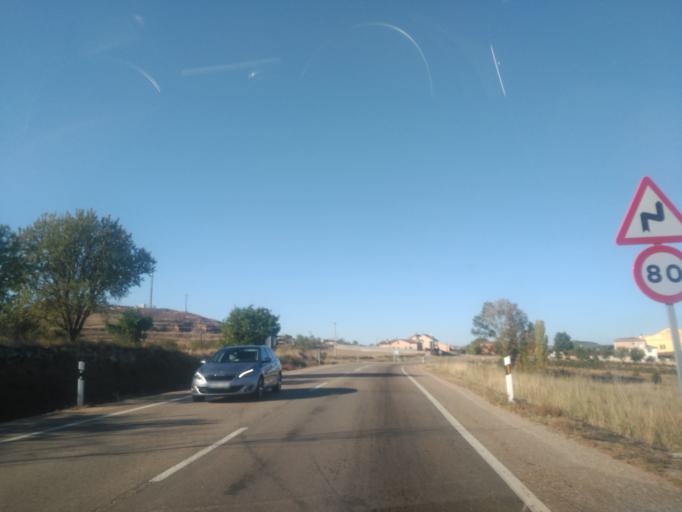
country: ES
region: Castille and Leon
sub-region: Provincia de Burgos
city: Castrillo de la Vega
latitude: 41.6544
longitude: -3.7729
